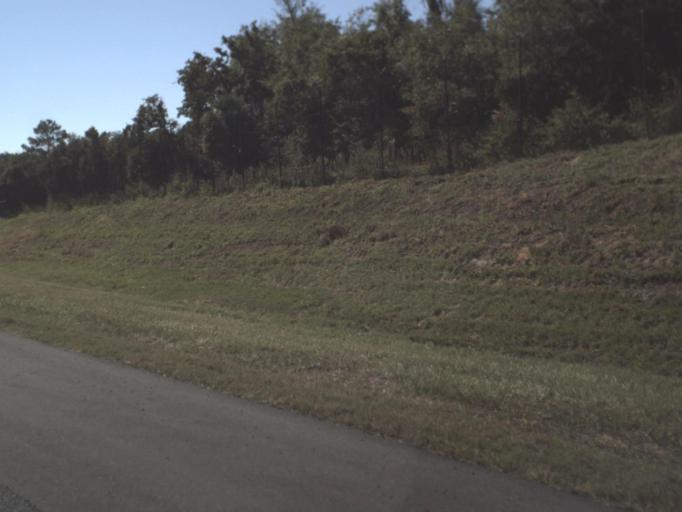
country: US
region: Florida
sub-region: Citrus County
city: Sugarmill Woods
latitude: 28.6427
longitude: -82.4898
